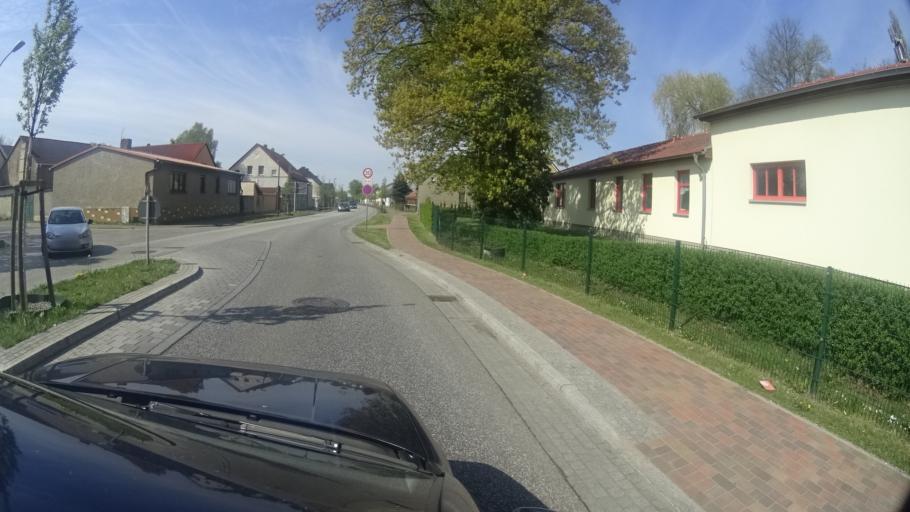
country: DE
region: Brandenburg
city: Nauen
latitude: 52.6203
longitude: 12.7950
